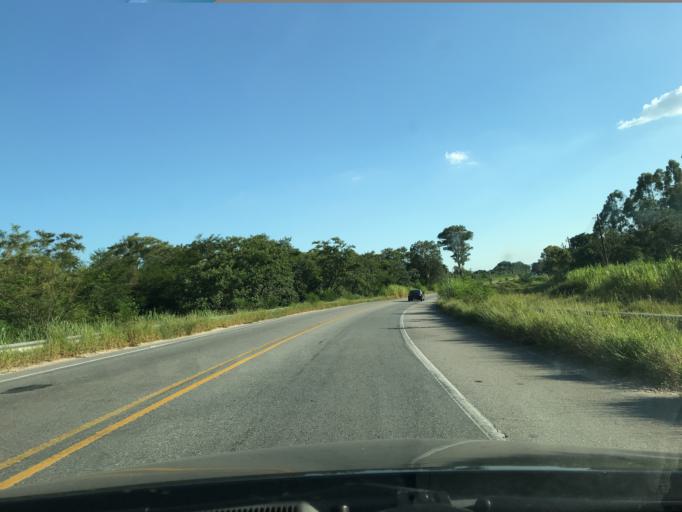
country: BR
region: Sao Paulo
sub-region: Taubate
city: Taubate
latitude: -23.0018
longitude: -45.6392
